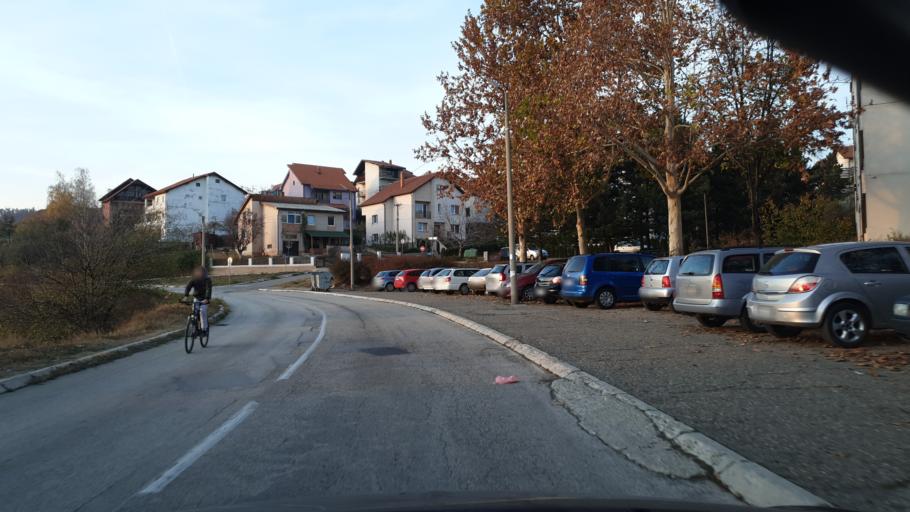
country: RS
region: Central Serbia
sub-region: Borski Okrug
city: Bor
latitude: 44.0584
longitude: 22.0944
